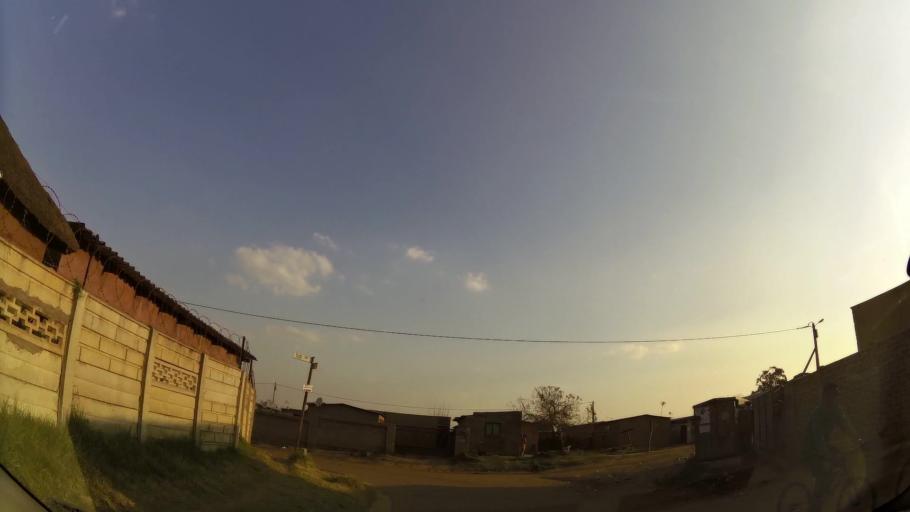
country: ZA
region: Gauteng
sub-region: Ekurhuleni Metropolitan Municipality
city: Benoni
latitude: -26.1548
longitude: 28.3796
